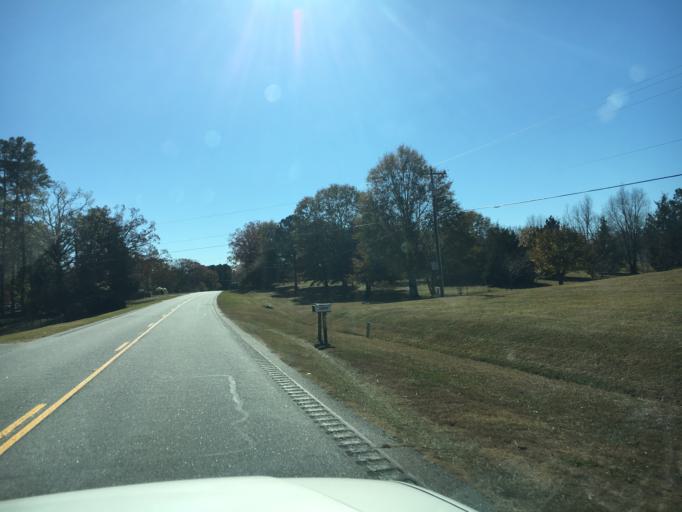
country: US
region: South Carolina
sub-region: Anderson County
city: Centerville
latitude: 34.4699
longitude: -82.7870
